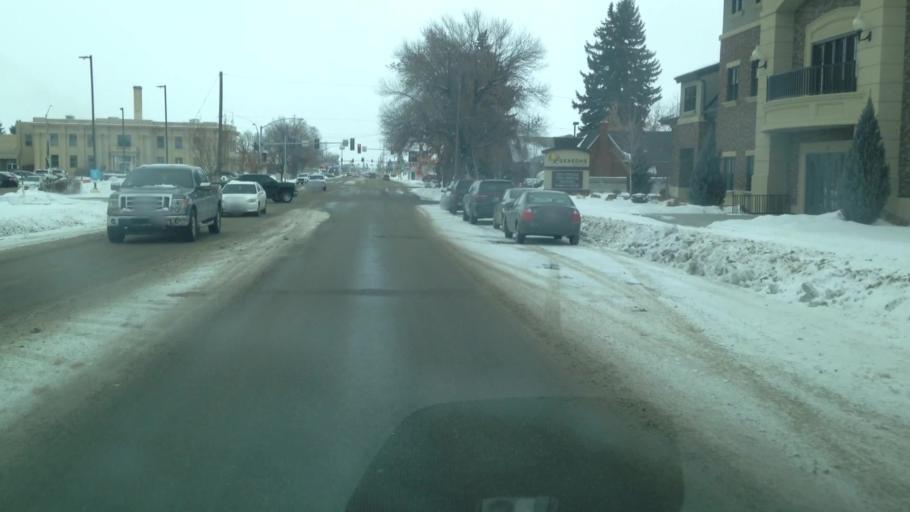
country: US
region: Idaho
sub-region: Madison County
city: Rexburg
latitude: 43.8247
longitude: -111.7781
